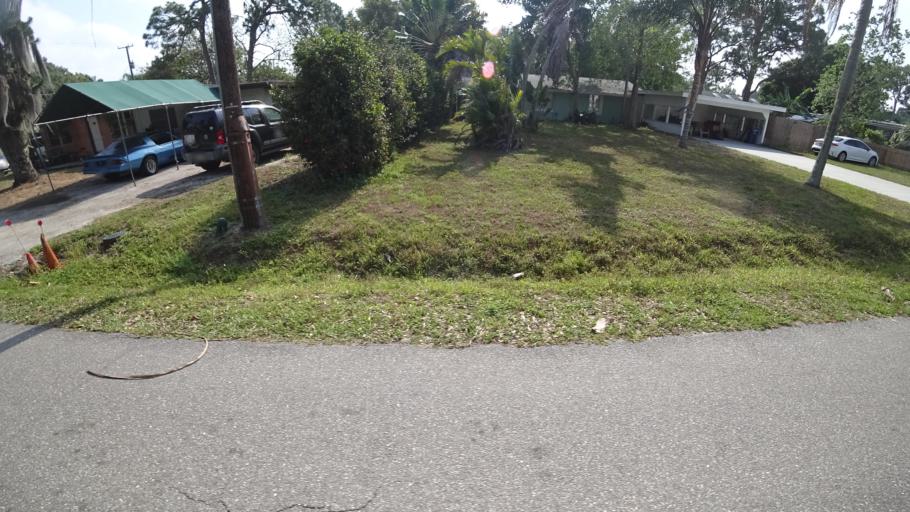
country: US
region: Florida
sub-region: Manatee County
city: West Bradenton
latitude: 27.4991
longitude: -82.6029
